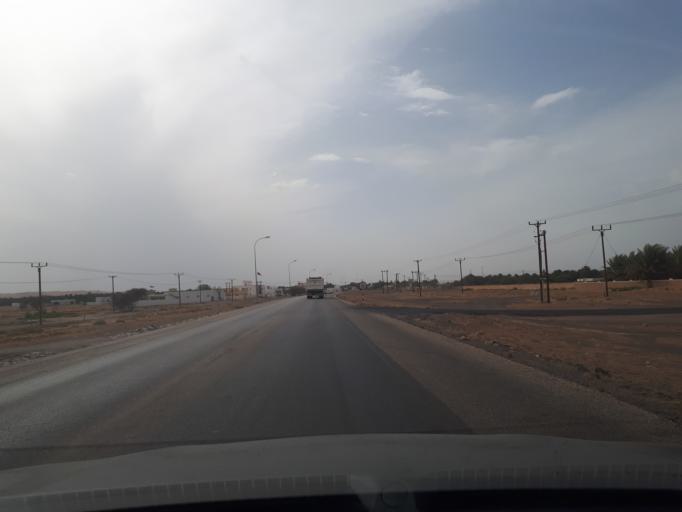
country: OM
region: Ash Sharqiyah
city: Badiyah
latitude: 22.4947
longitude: 58.7567
